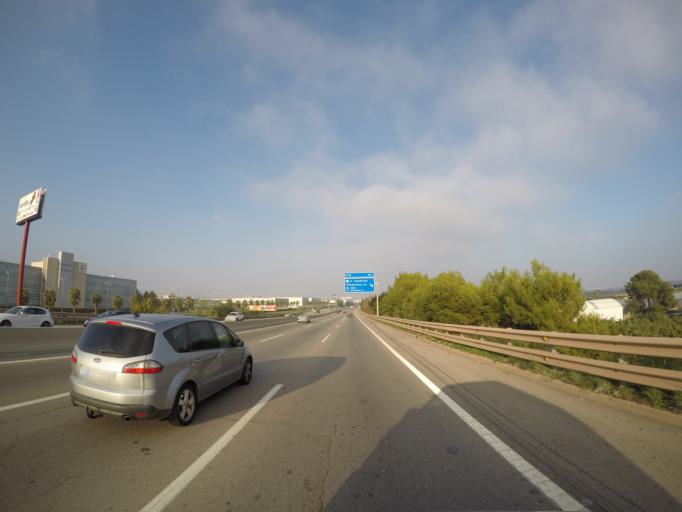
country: ES
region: Catalonia
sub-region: Provincia de Barcelona
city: Viladecans
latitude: 41.3132
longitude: 2.0328
